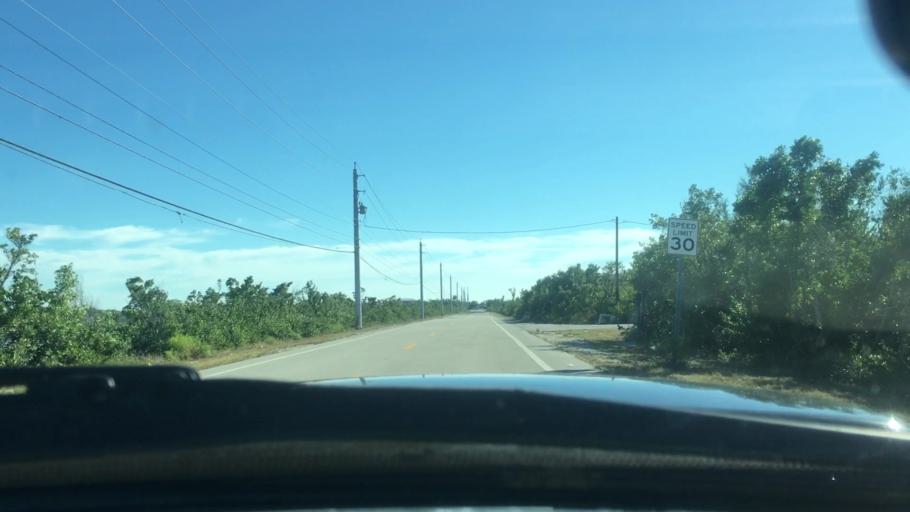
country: US
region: Florida
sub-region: Monroe County
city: Cudjoe Key
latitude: 24.6731
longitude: -81.4997
